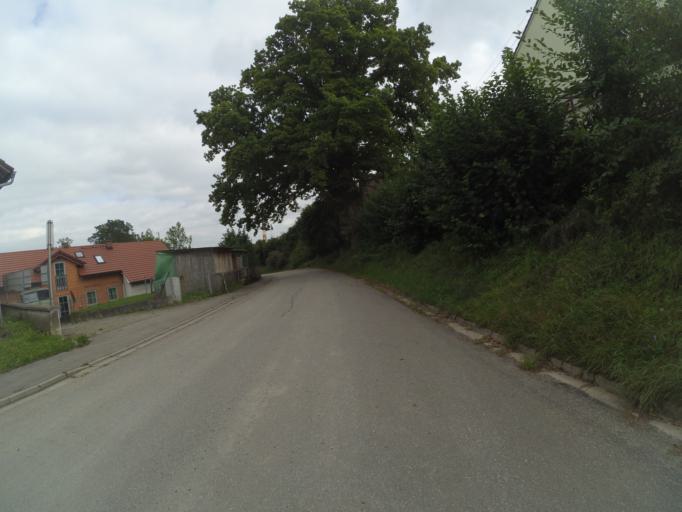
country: DE
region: Bavaria
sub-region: Upper Bavaria
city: Hurlach
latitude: 48.0711
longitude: 10.8083
